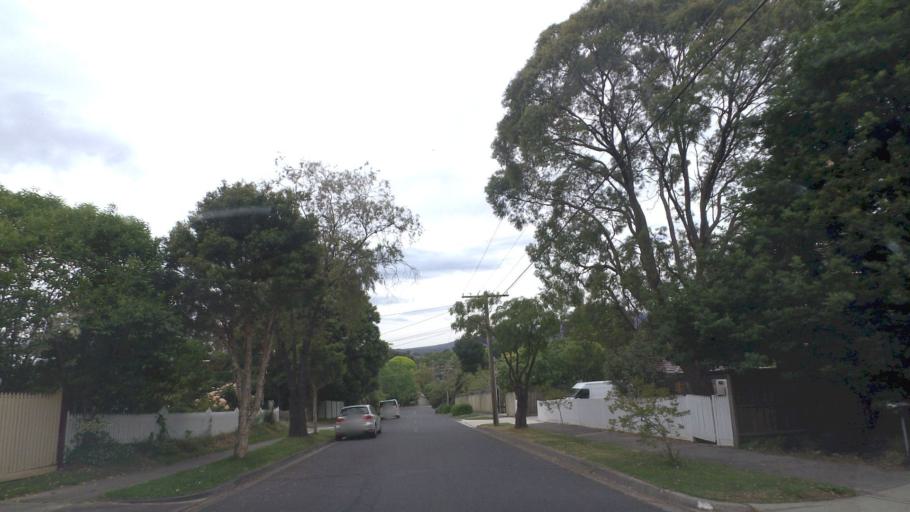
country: AU
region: Victoria
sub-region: Maroondah
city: Croydon North
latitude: -37.7919
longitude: 145.2954
